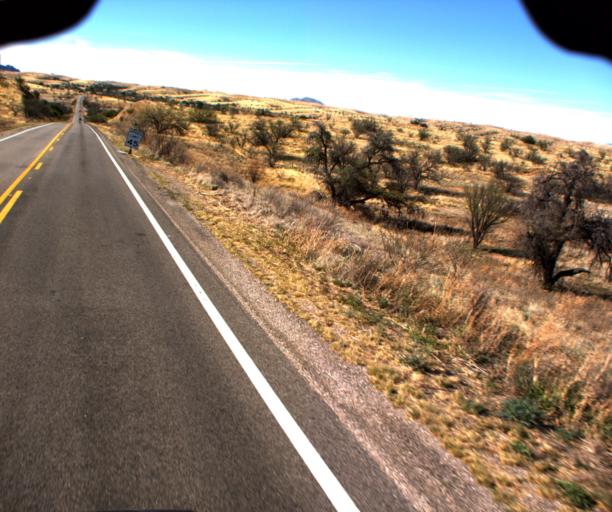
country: US
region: Arizona
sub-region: Pima County
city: Corona de Tucson
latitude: 31.7753
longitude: -110.6876
